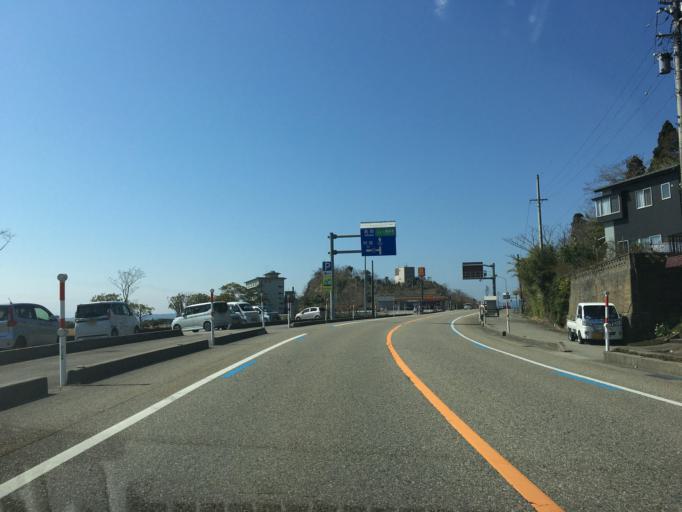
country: JP
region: Toyama
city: Himi
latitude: 36.8882
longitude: 136.9983
